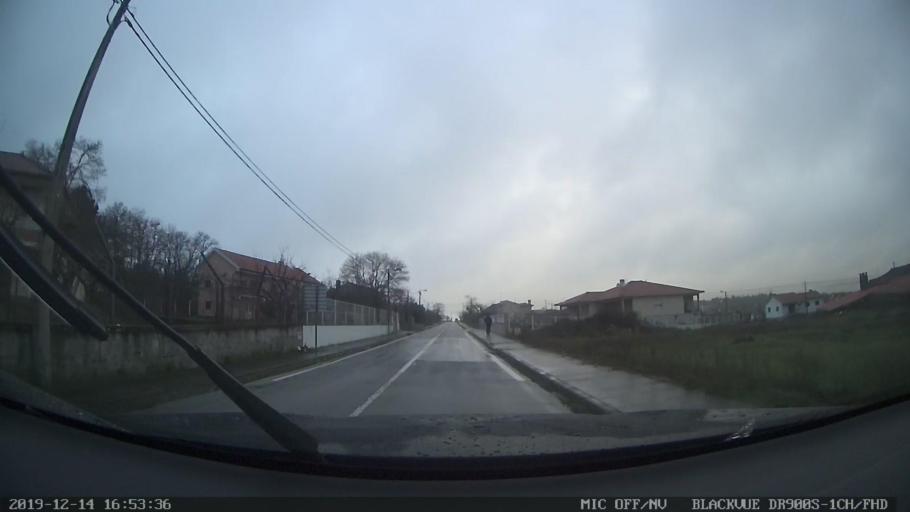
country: PT
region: Vila Real
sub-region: Murca
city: Murca
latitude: 41.4322
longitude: -7.5177
